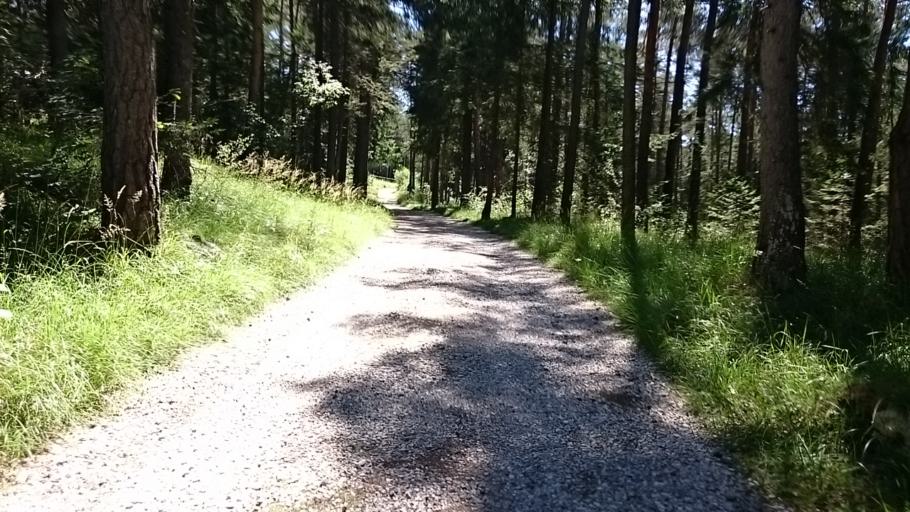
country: IT
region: Veneto
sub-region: Provincia di Belluno
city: San Vito
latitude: 46.4947
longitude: 12.1786
